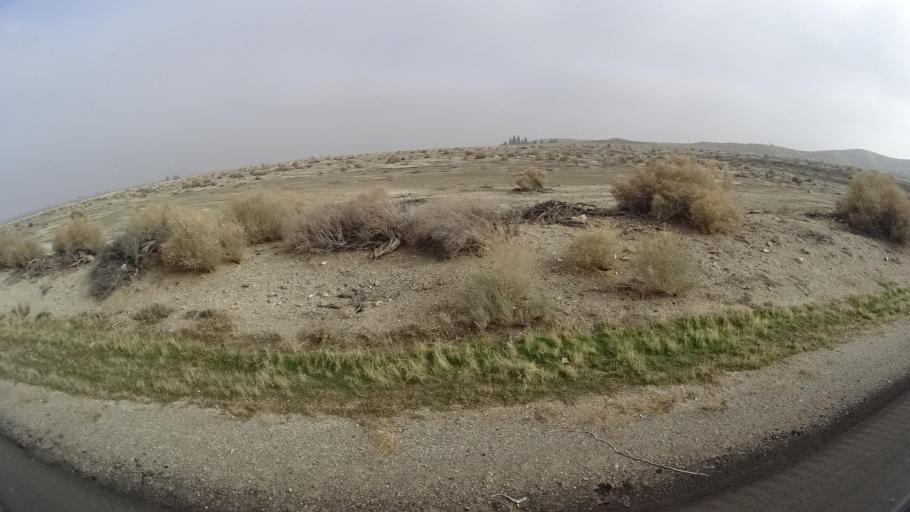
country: US
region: California
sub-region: Kern County
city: Maricopa
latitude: 35.0415
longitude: -119.3670
